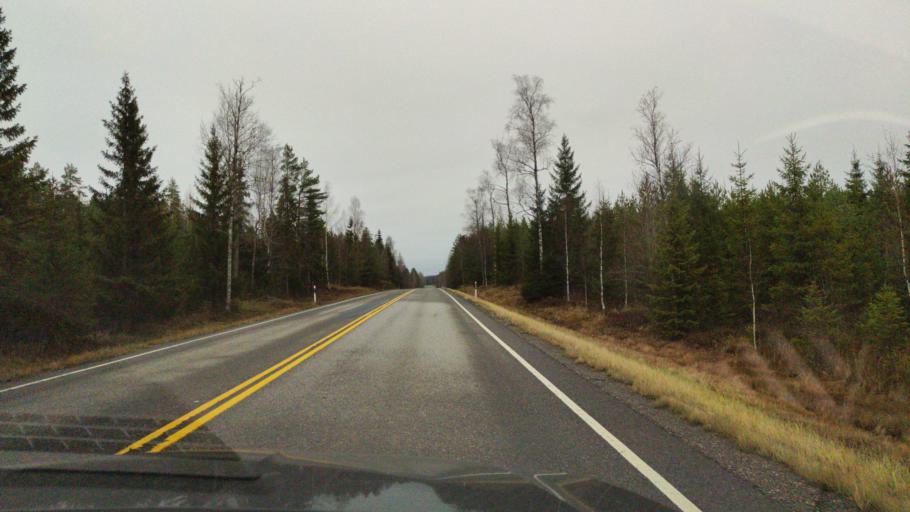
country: FI
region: Varsinais-Suomi
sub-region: Loimaa
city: Ylaene
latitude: 60.7708
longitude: 22.4382
